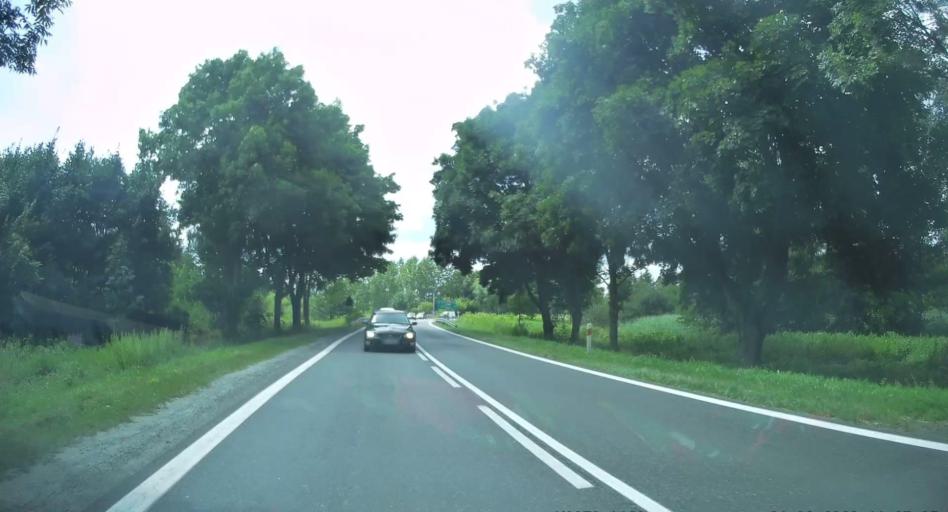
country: PL
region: Subcarpathian Voivodeship
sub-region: Powiat tarnobrzeski
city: Baranow Sandomierski
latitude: 50.4871
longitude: 21.5679
